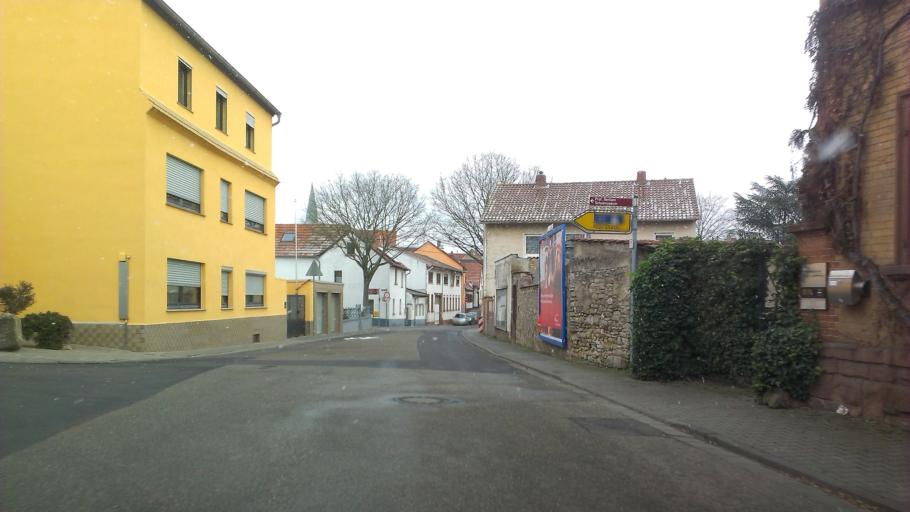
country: DE
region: Rheinland-Pfalz
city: Morstadt
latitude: 49.6375
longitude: 8.2711
